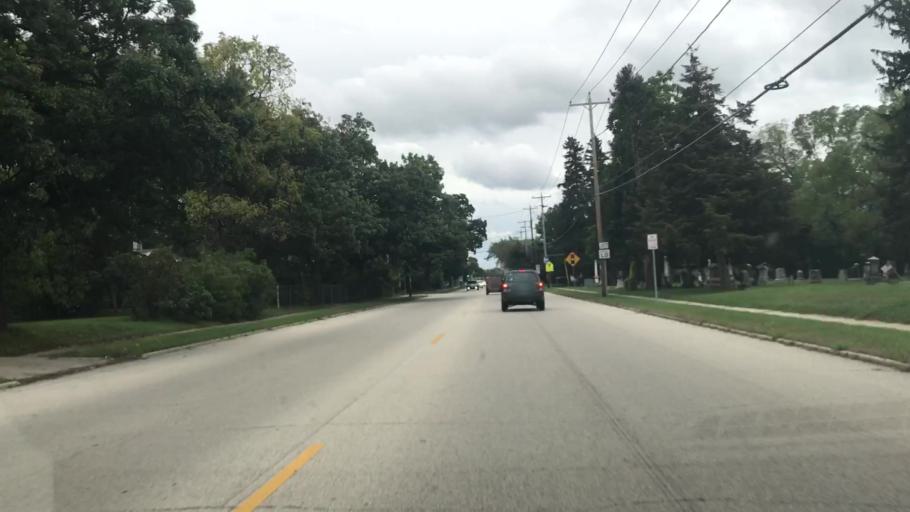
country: US
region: Wisconsin
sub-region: Waukesha County
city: Mukwonago
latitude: 42.8681
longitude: -88.3349
